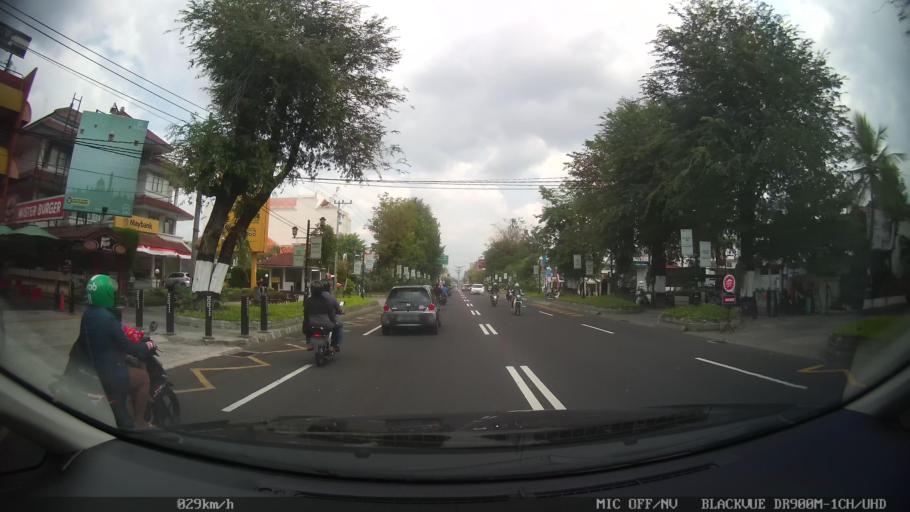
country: ID
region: Daerah Istimewa Yogyakarta
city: Yogyakarta
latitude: -7.7832
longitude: 110.3734
